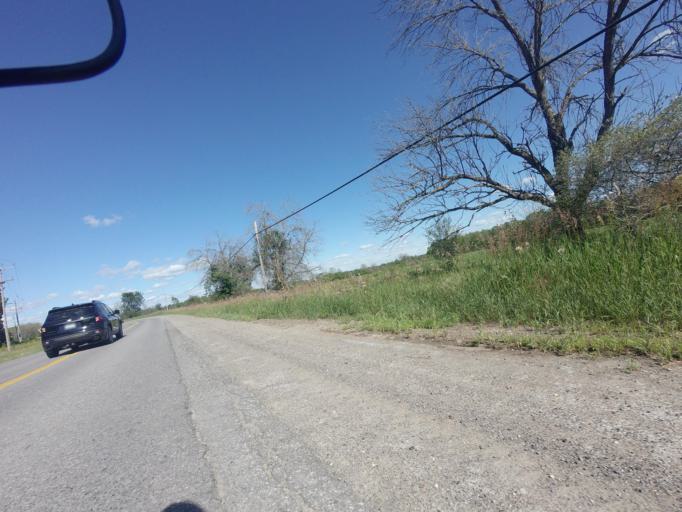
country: CA
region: Ontario
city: Arnprior
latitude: 45.4122
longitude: -76.4365
